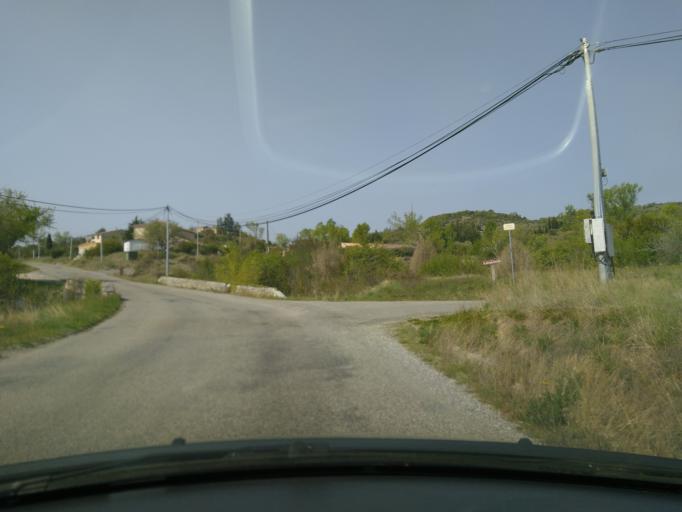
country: FR
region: Rhone-Alpes
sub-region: Departement de l'Ardeche
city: Ruoms
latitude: 44.4590
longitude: 4.4046
